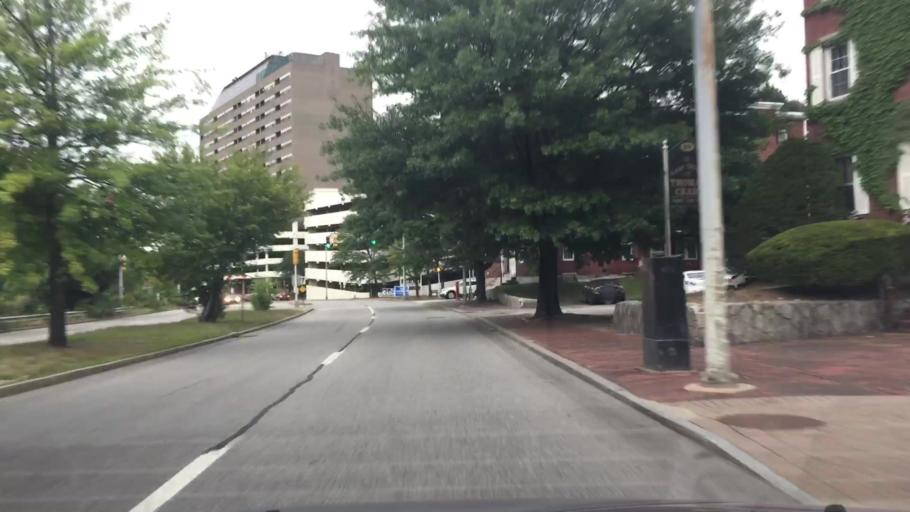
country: US
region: New Hampshire
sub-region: Hillsborough County
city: Manchester
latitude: 42.9916
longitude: -71.4662
